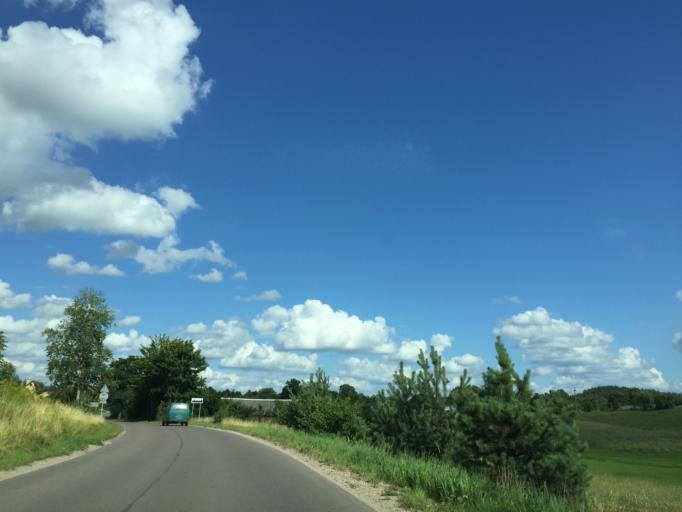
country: PL
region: Podlasie
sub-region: Suwalki
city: Suwalki
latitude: 54.1134
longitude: 22.9824
